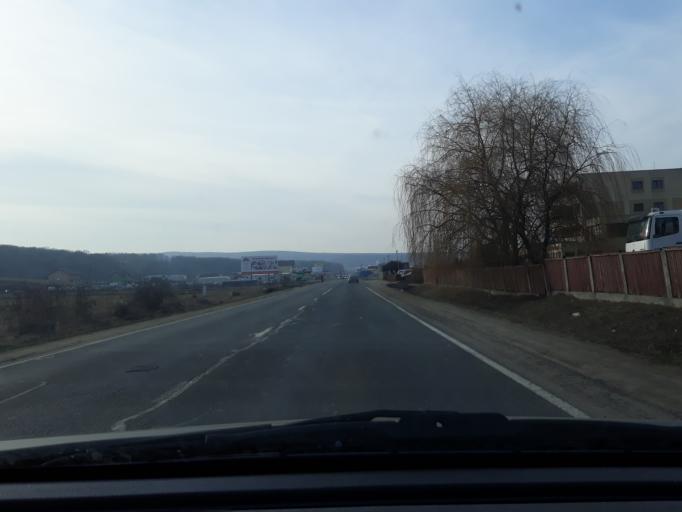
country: RO
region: Salaj
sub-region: Comuna Criseni
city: Criseni
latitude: 47.2239
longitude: 23.0284
